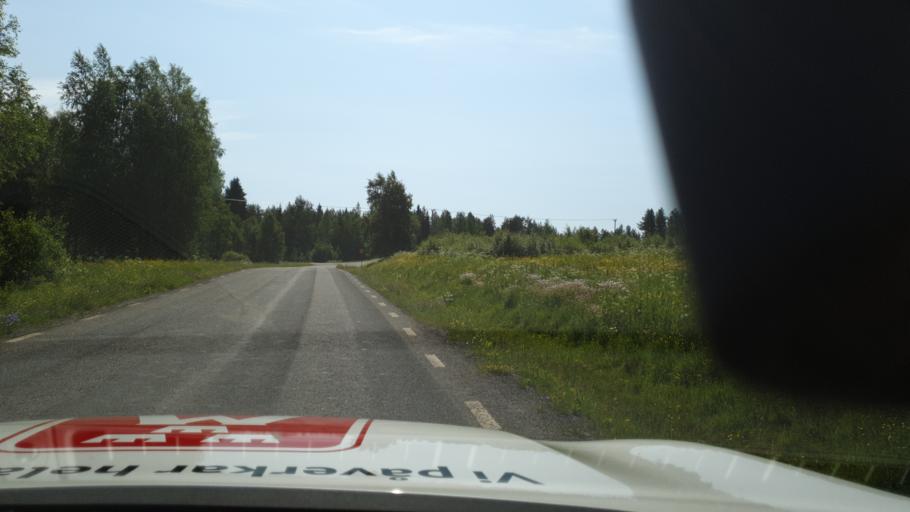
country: SE
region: Vaesterbotten
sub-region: Skelleftea Kommun
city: Langsele
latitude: 65.0063
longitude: 20.0883
